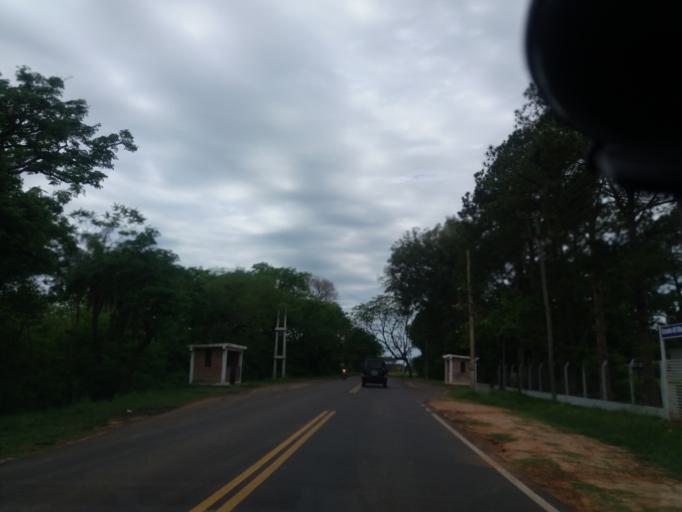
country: AR
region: Corrientes
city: Corrientes
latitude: -27.4526
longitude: -58.7246
